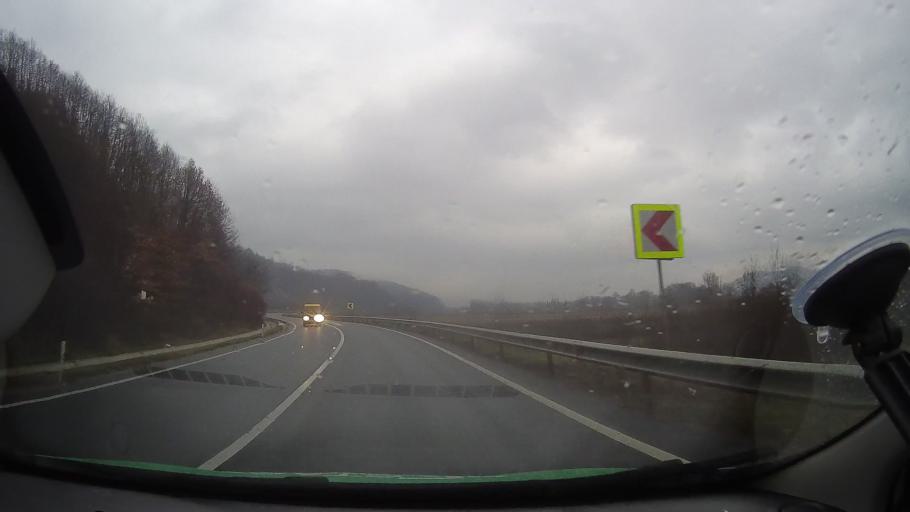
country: RO
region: Hunedoara
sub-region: Comuna Tomesti
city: Tomesti
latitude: 46.1830
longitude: 22.6505
